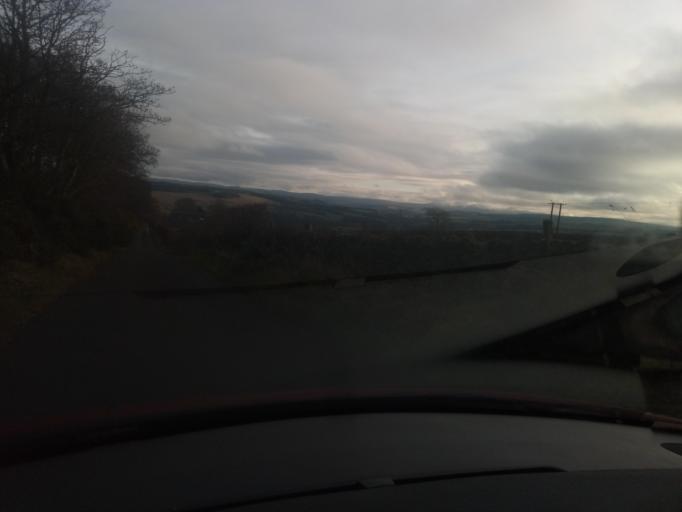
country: GB
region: Scotland
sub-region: The Scottish Borders
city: Jedburgh
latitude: 55.4797
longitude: -2.5708
